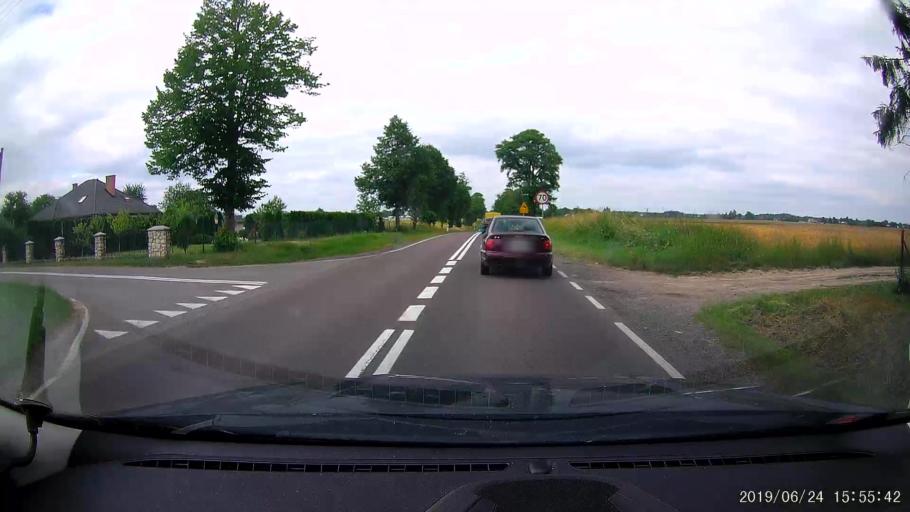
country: PL
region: Subcarpathian Voivodeship
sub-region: Powiat lubaczowski
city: Cieszanow
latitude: 50.2322
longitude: 23.1242
